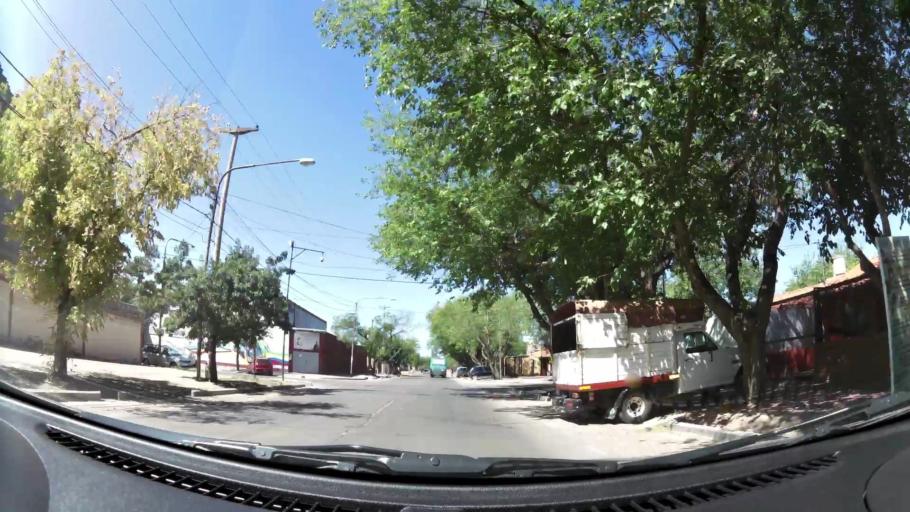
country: AR
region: Mendoza
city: Mendoza
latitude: -32.8859
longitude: -68.8040
